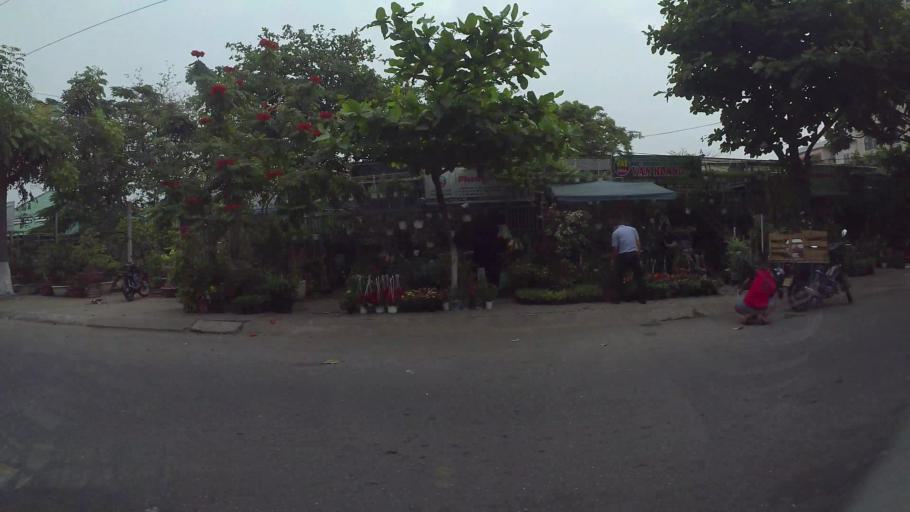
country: VN
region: Da Nang
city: Cam Le
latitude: 16.0359
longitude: 108.2183
